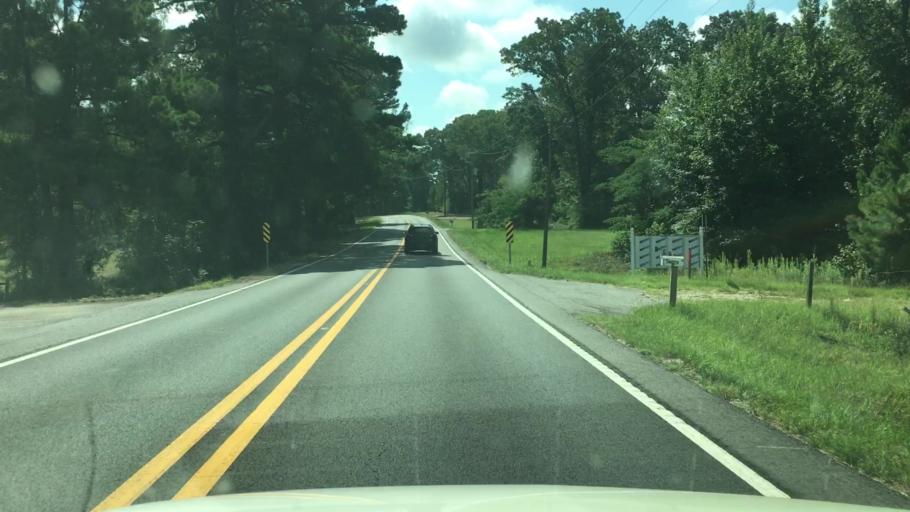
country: US
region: Arkansas
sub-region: Garland County
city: Lake Hamilton
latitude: 34.2802
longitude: -93.1595
